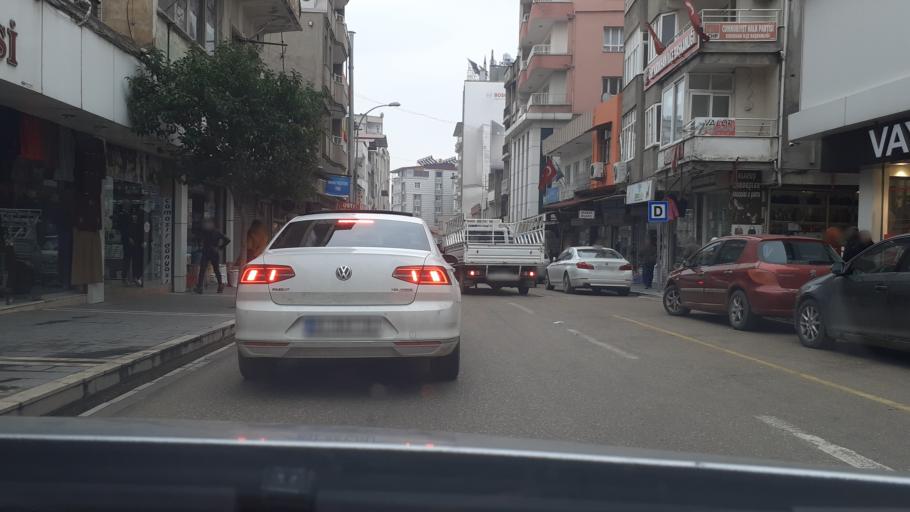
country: TR
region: Hatay
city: Kirikhan
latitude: 36.4987
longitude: 36.3565
